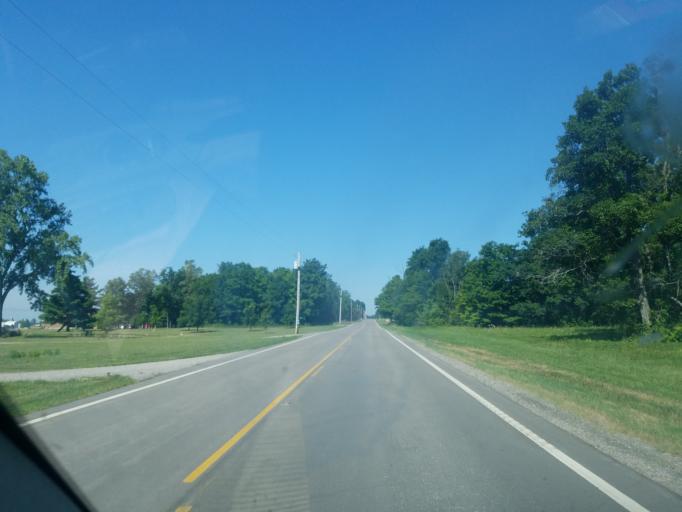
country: US
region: Ohio
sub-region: Logan County
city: Northwood
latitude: 40.4526
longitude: -83.7514
